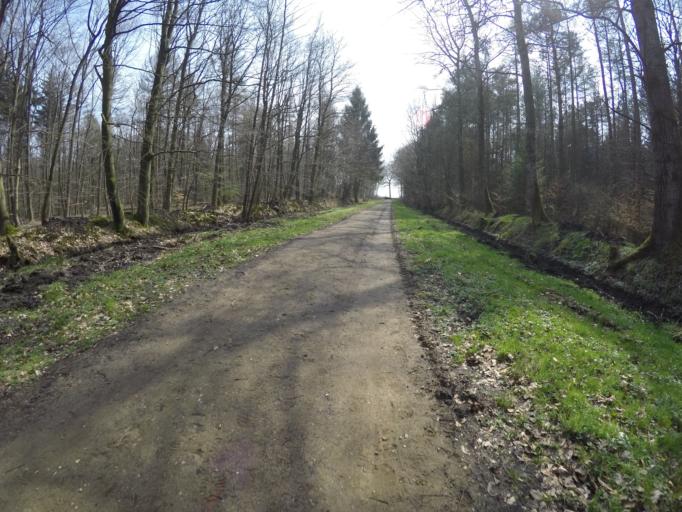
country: DE
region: Schleswig-Holstein
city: Borstel-Hohenraden
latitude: 53.7209
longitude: 9.8061
